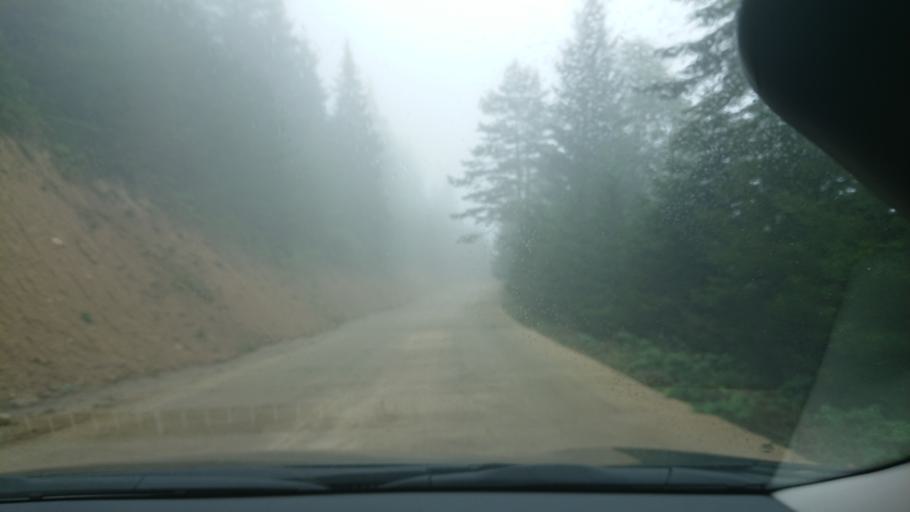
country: TR
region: Gumushane
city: Kurtun
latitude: 40.6628
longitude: 39.0165
